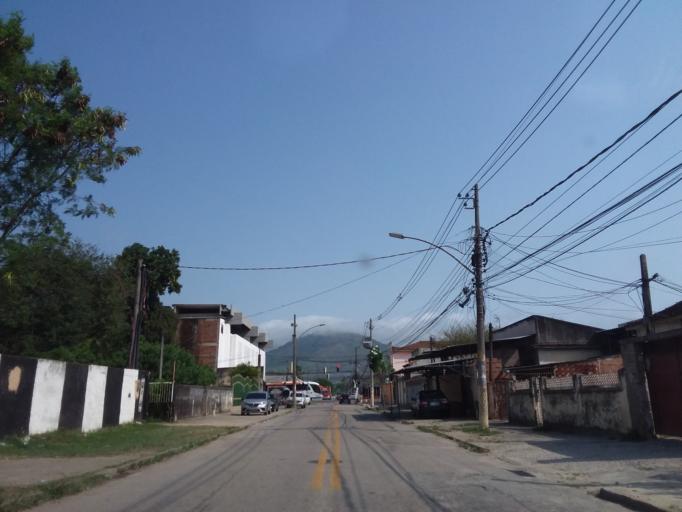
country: BR
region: Rio de Janeiro
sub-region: Nilopolis
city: Nilopolis
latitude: -22.9008
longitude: -43.5464
